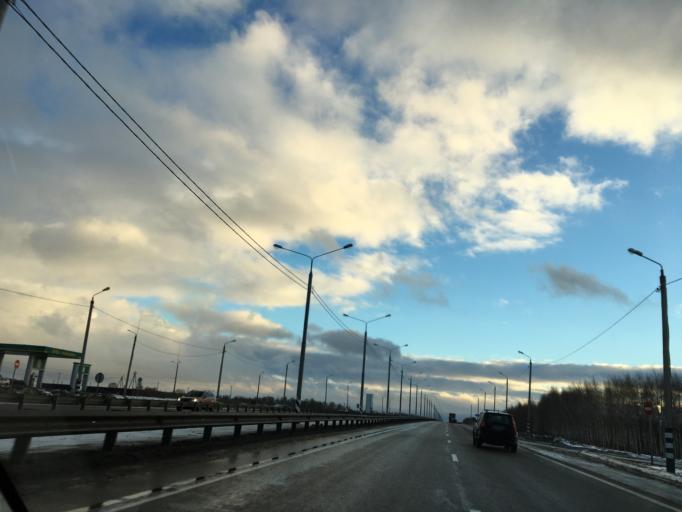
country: RU
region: Tula
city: Zaokskiy
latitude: 54.8052
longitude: 37.4838
